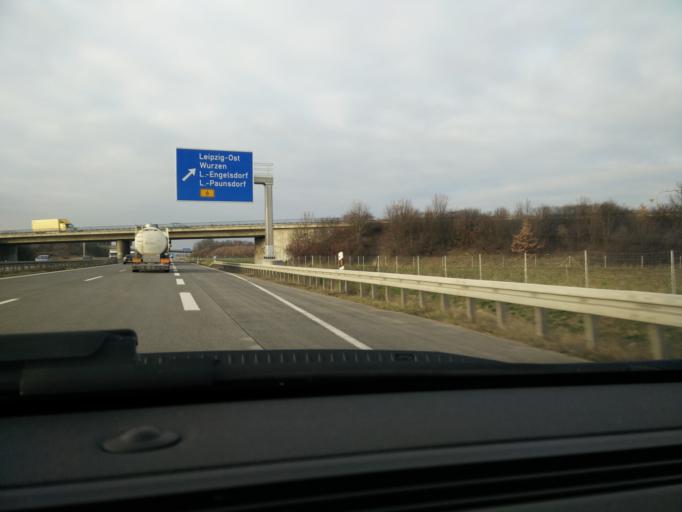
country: DE
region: Saxony
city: Taucha
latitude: 51.3548
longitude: 12.4958
